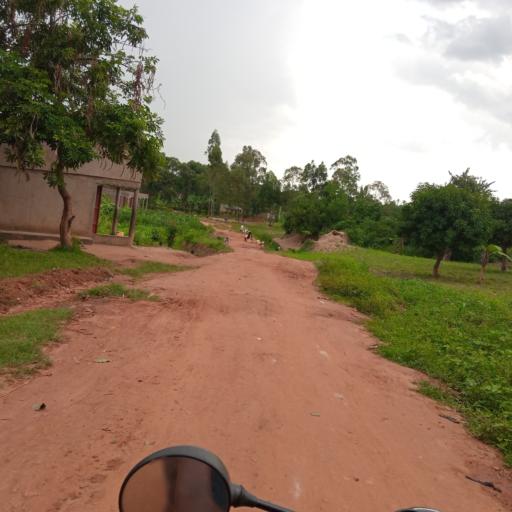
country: UG
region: Eastern Region
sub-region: Mbale District
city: Mbale
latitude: 1.1249
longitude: 34.1756
